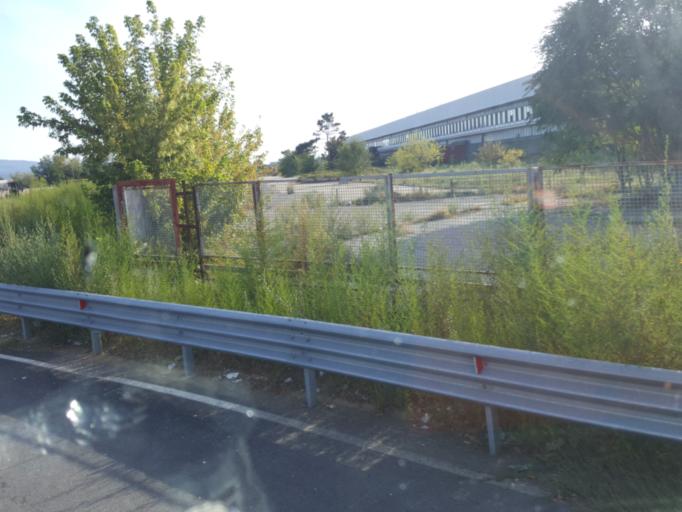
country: IT
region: Piedmont
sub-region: Provincia di Torino
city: Settimo Torinese
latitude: 45.1402
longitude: 7.7403
